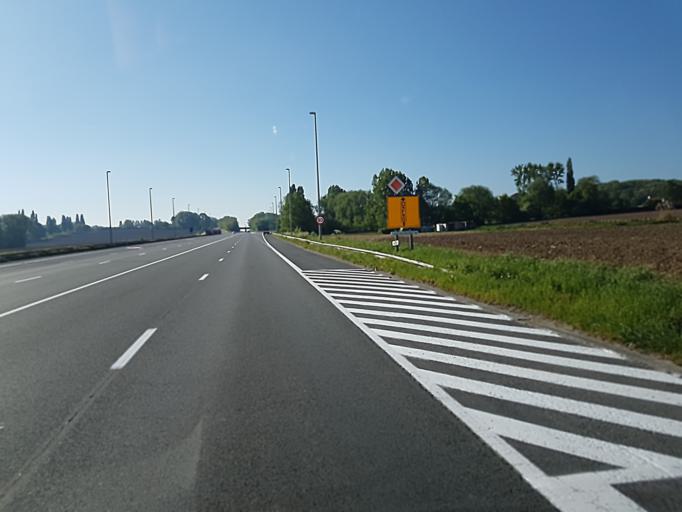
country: BE
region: Wallonia
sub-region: Province du Hainaut
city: Mouscron
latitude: 50.7655
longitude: 3.1946
